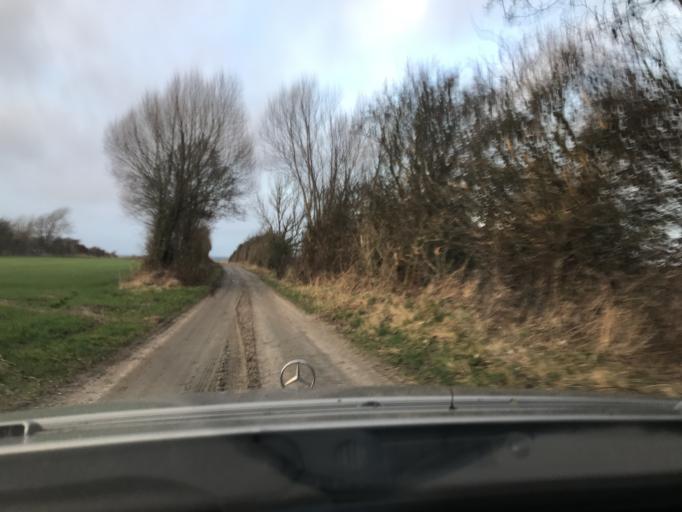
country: DK
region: South Denmark
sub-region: Sonderborg Kommune
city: Nordborg
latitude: 55.0635
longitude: 9.6690
